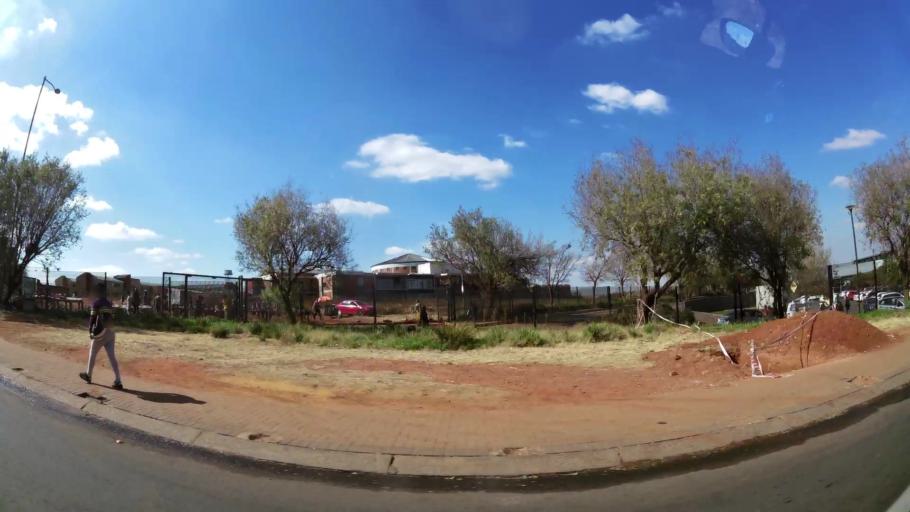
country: ZA
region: Gauteng
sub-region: West Rand District Municipality
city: Krugersdorp
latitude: -26.1651
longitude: 27.7796
